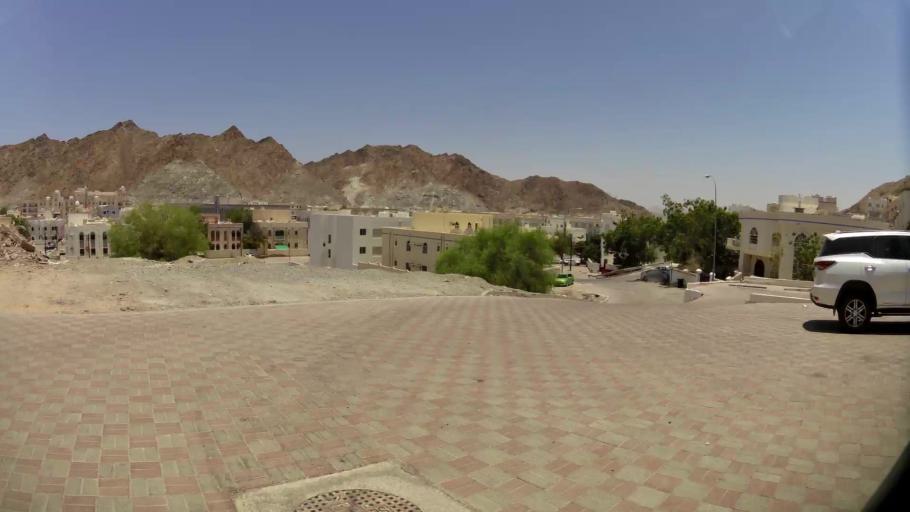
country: OM
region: Muhafazat Masqat
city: Muscat
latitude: 23.6288
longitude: 58.5388
